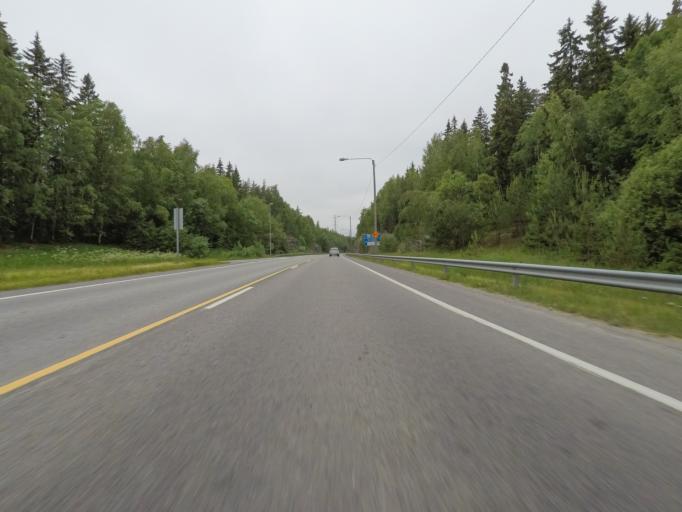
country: FI
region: Varsinais-Suomi
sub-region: Turku
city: Raisio
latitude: 60.4621
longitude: 22.1477
